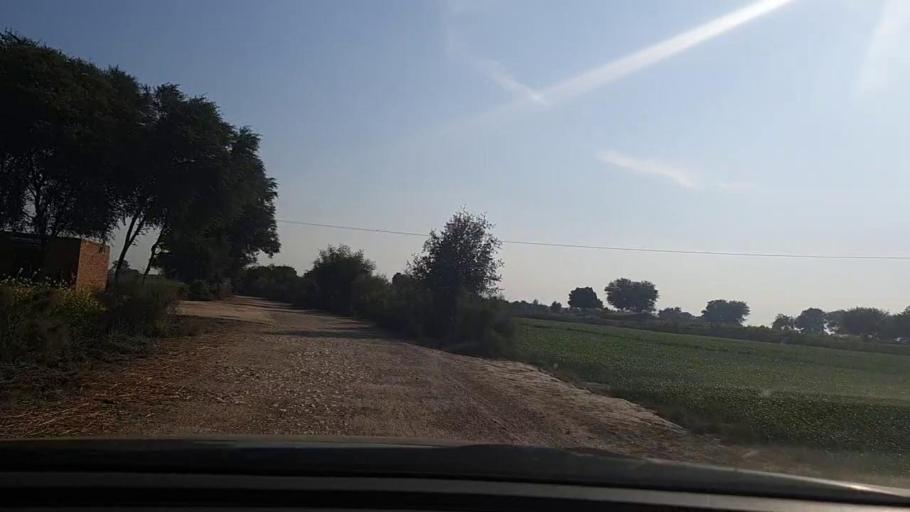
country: PK
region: Sindh
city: Sehwan
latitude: 26.3066
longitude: 68.0012
